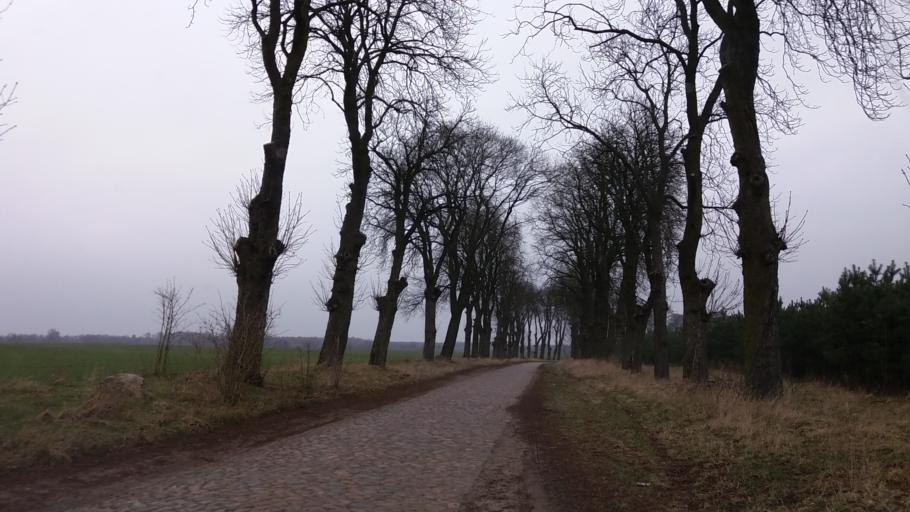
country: PL
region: West Pomeranian Voivodeship
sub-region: Powiat choszczenski
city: Choszczno
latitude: 53.1805
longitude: 15.3274
